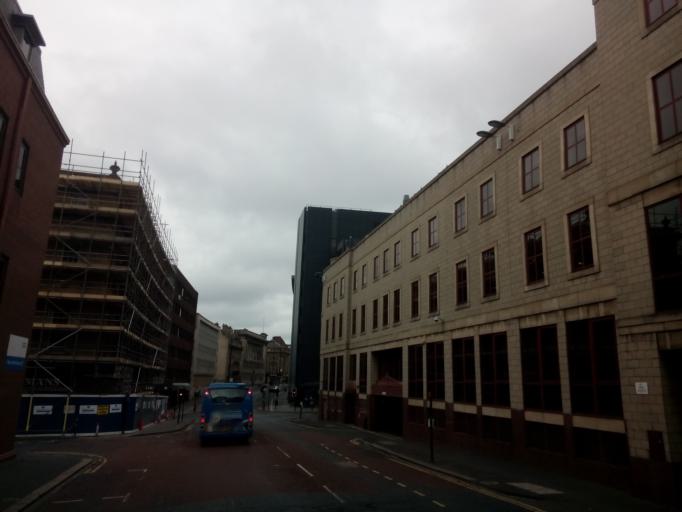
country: GB
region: England
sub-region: Newcastle upon Tyne
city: Newcastle upon Tyne
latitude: 54.9747
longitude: -1.6080
